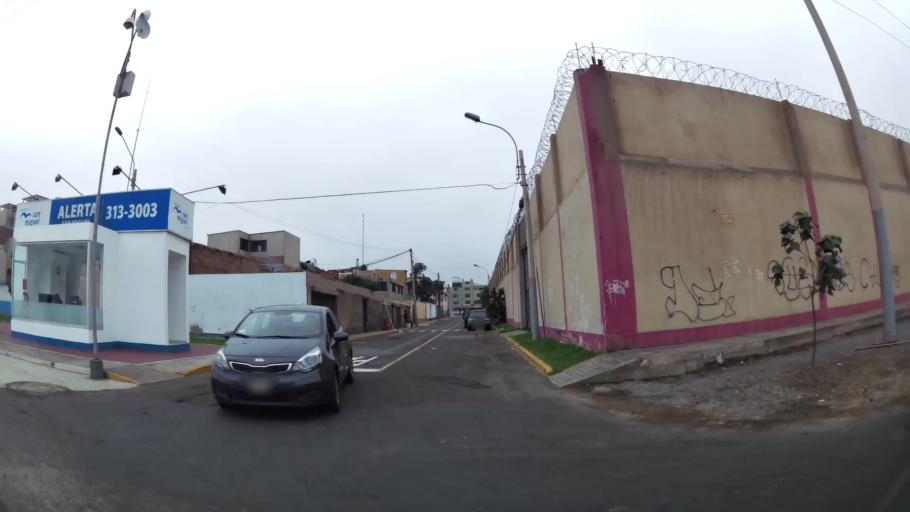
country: PE
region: Callao
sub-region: Callao
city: Callao
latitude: -12.0833
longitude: -77.1016
